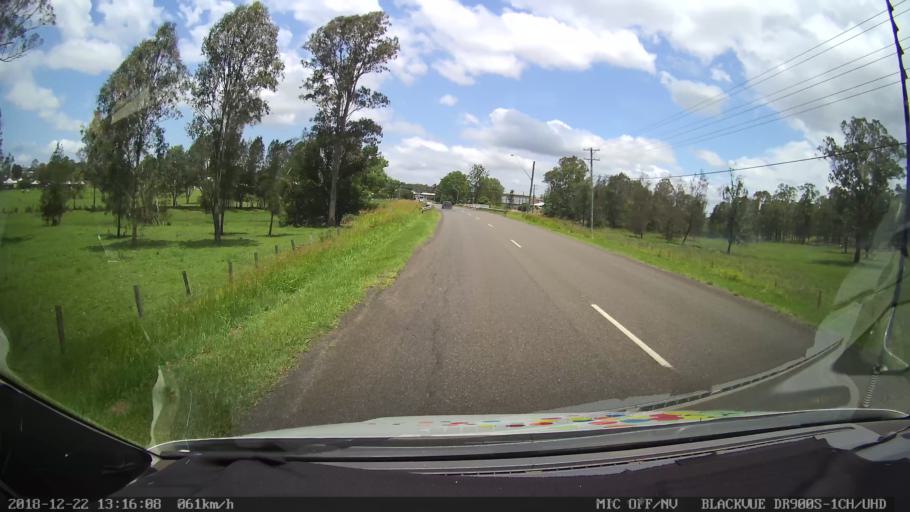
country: AU
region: New South Wales
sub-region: Clarence Valley
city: South Grafton
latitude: -29.7236
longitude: 152.9386
